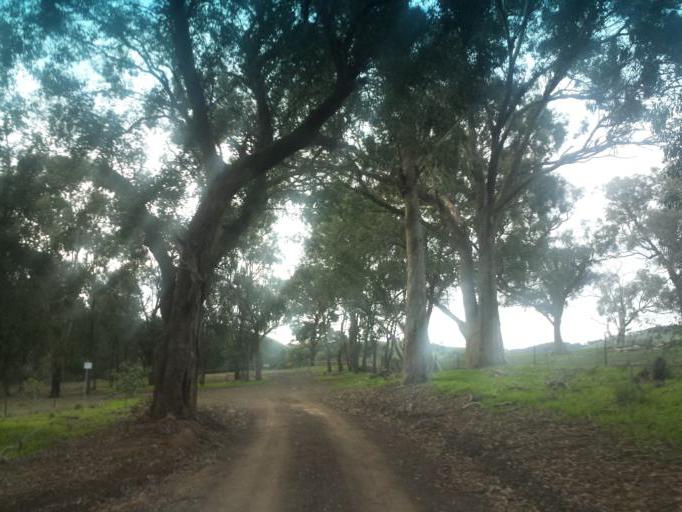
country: AU
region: Victoria
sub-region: Murrindindi
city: Kinglake West
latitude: -37.0147
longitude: 145.2502
